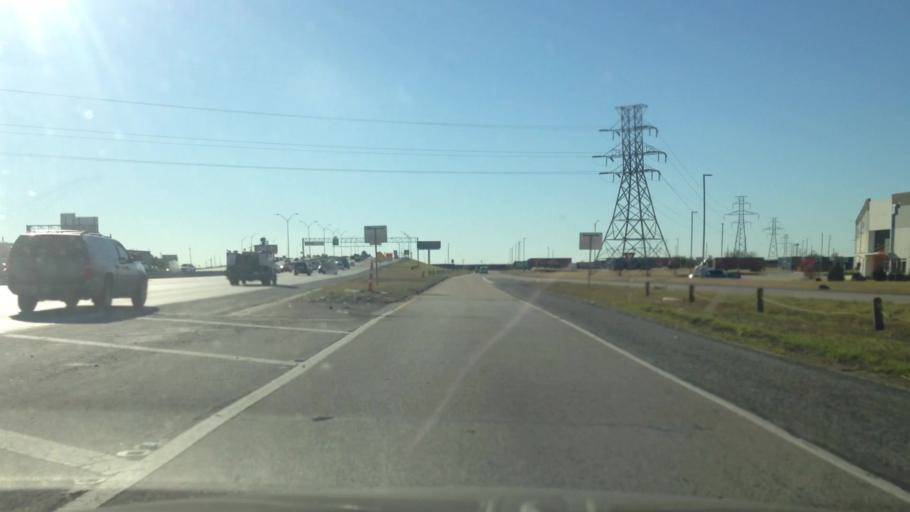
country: US
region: Texas
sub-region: Tarrant County
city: Blue Mound
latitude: 32.8410
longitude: -97.3522
